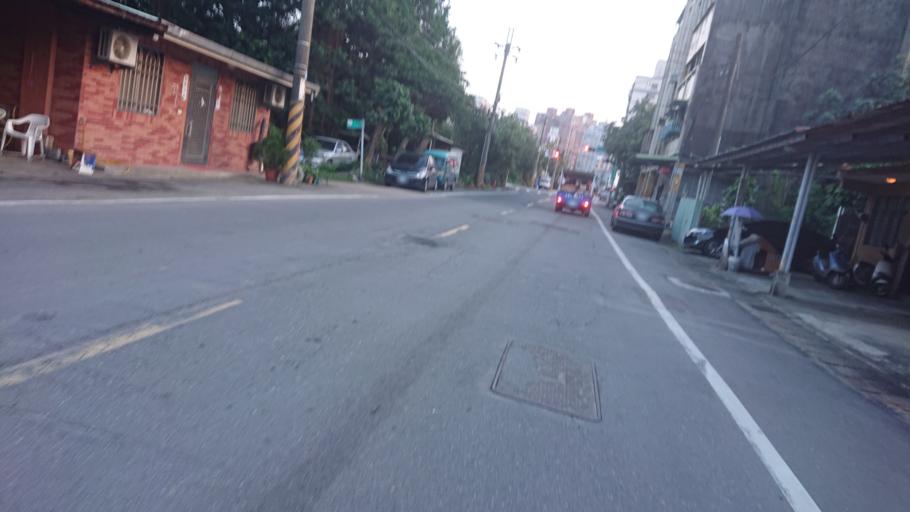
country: TW
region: Taipei
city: Taipei
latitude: 25.1877
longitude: 121.4201
